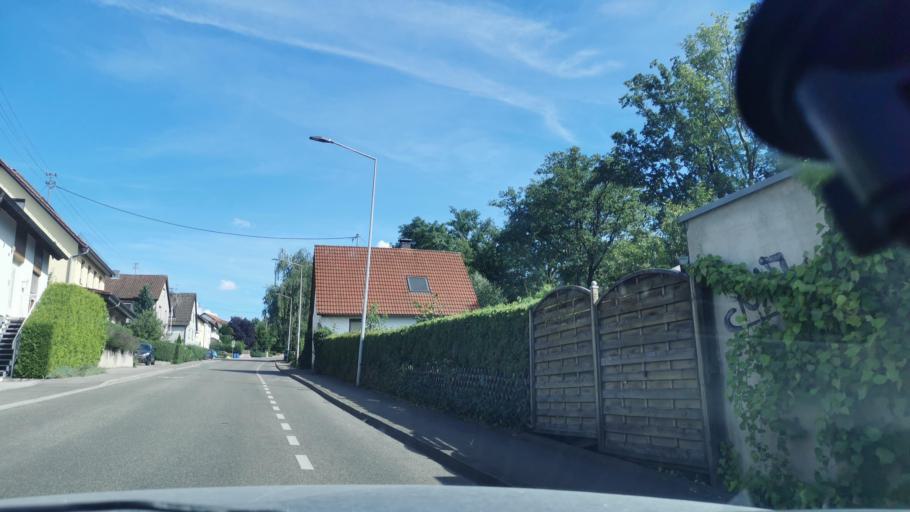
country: DE
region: Baden-Wuerttemberg
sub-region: Regierungsbezirk Stuttgart
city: Waldstetten
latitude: 48.7830
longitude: 9.8436
